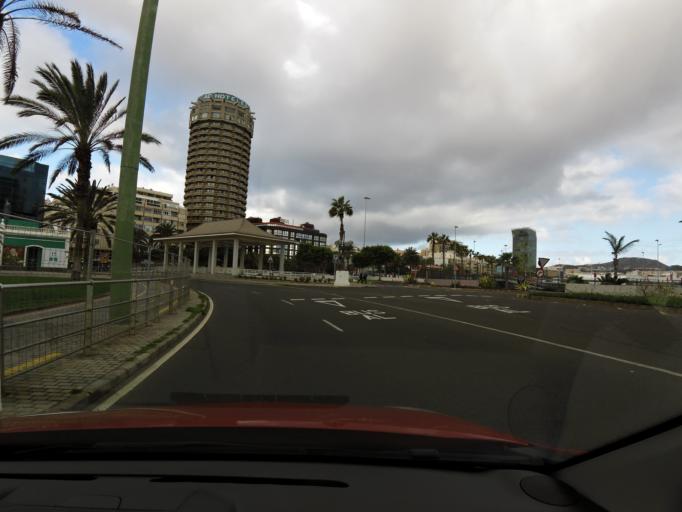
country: ES
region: Canary Islands
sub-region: Provincia de Las Palmas
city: Las Palmas de Gran Canaria
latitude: 28.1413
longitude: -15.4288
